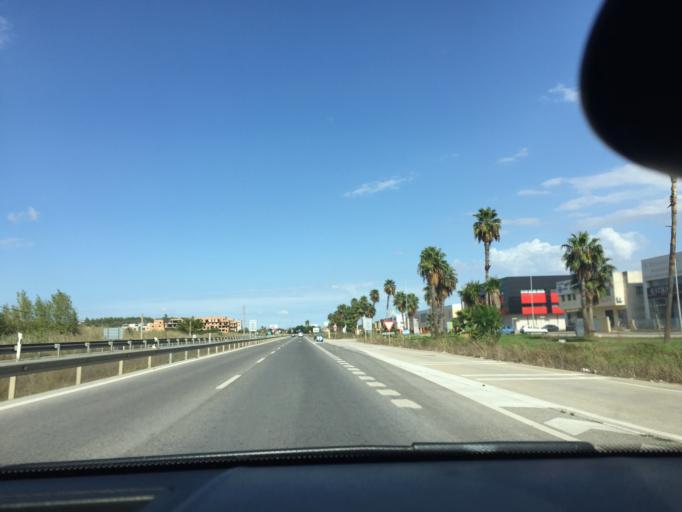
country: ES
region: Andalusia
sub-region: Provincia de Sevilla
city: Gelves
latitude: 37.3191
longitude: -6.0331
